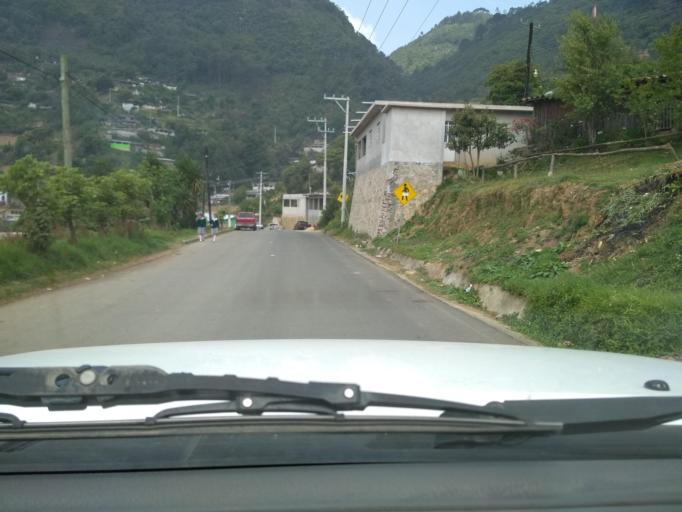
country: MX
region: Veracruz
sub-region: Camerino Z. Mendoza
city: Necoxtla
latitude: 18.7787
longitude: -97.1531
